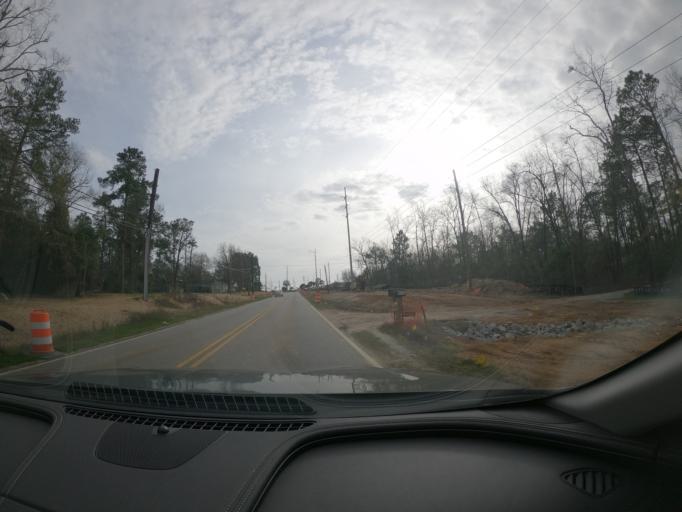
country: US
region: Georgia
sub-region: Columbia County
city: Martinez
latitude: 33.4936
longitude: -82.1097
